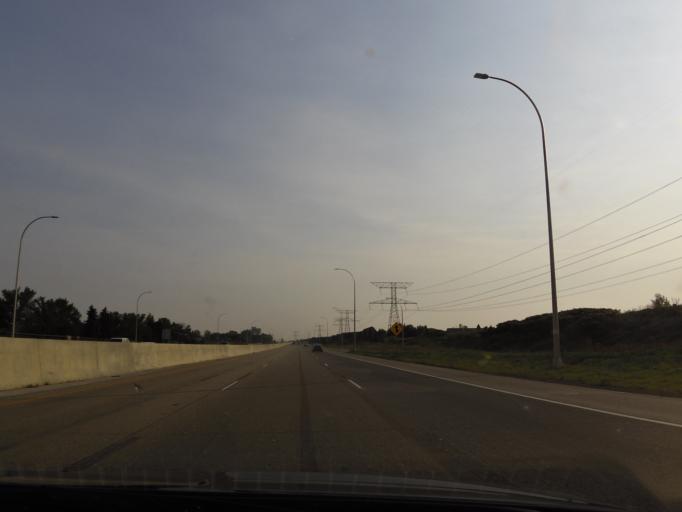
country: US
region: Minnesota
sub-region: Hennepin County
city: Maple Grove
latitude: 45.0657
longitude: -93.4484
